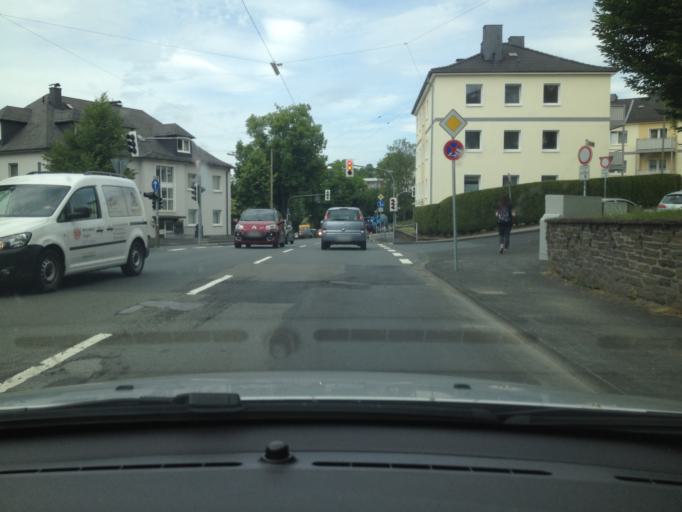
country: DE
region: North Rhine-Westphalia
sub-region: Regierungsbezirk Arnsberg
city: Siegen
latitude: 50.8770
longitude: 8.0319
